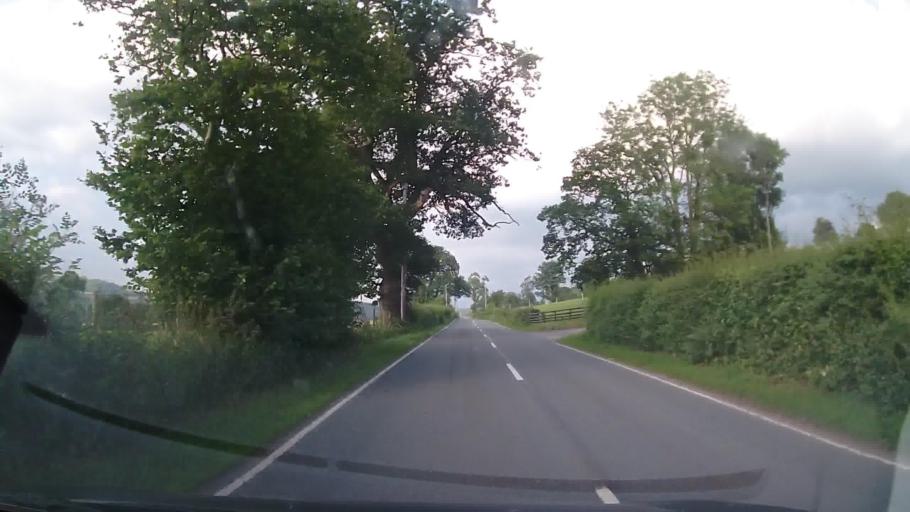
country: GB
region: Wales
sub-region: Gwynedd
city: Bala
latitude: 52.9044
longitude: -3.5769
